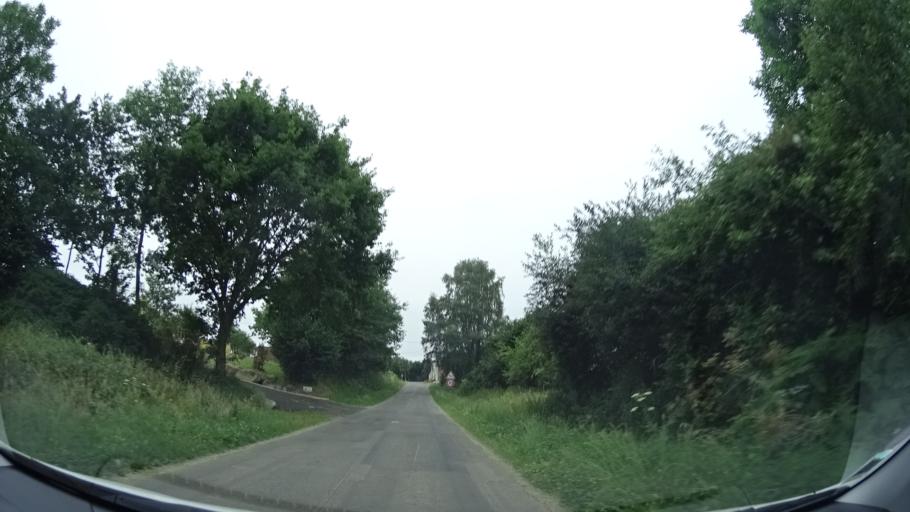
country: FR
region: Brittany
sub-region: Departement d'Ille-et-Vilaine
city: Irodouer
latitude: 48.3188
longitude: -1.9331
